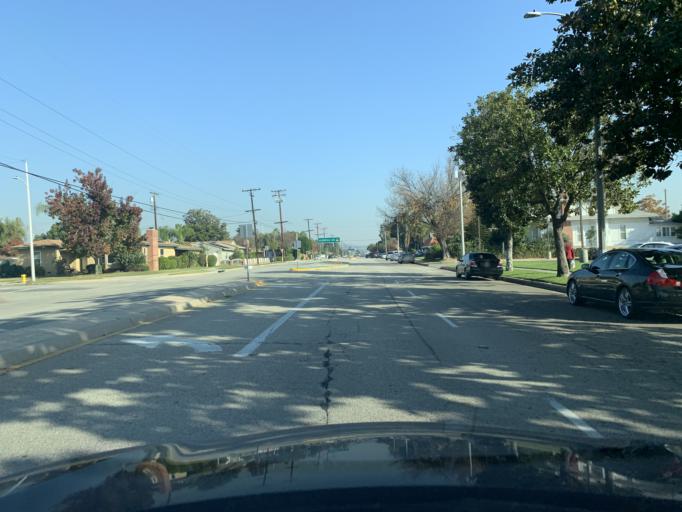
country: US
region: California
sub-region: Los Angeles County
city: Covina
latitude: 34.0790
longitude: -117.8967
